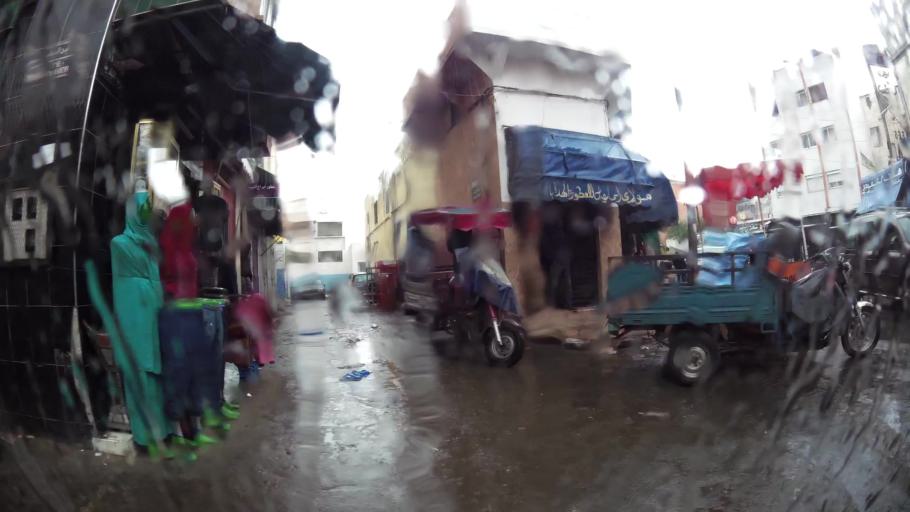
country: MA
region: Grand Casablanca
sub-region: Casablanca
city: Casablanca
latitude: 33.5764
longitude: -7.6042
